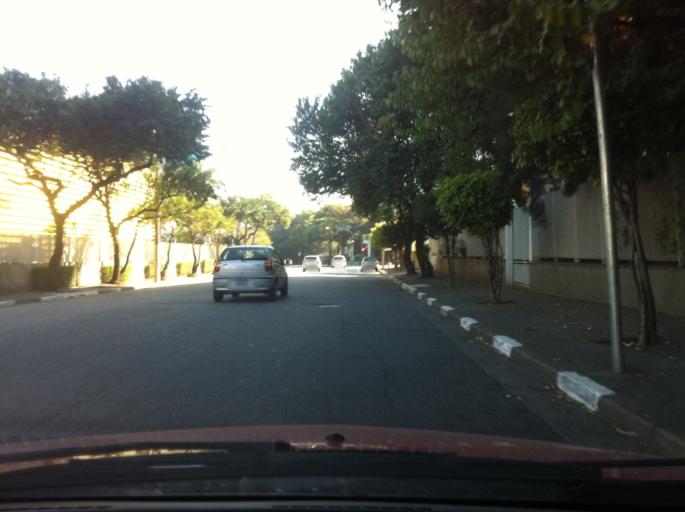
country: BR
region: Sao Paulo
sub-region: Sao Paulo
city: Sao Paulo
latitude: -23.6047
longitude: -46.6496
